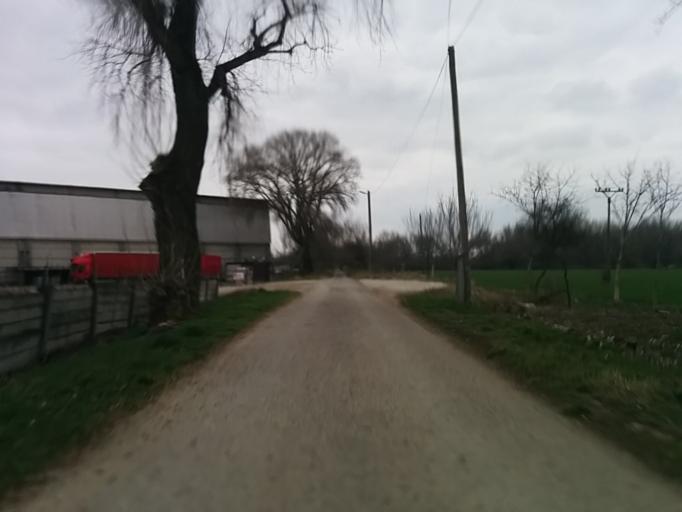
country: SK
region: Nitriansky
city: Sellye
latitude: 48.2418
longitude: 17.8242
